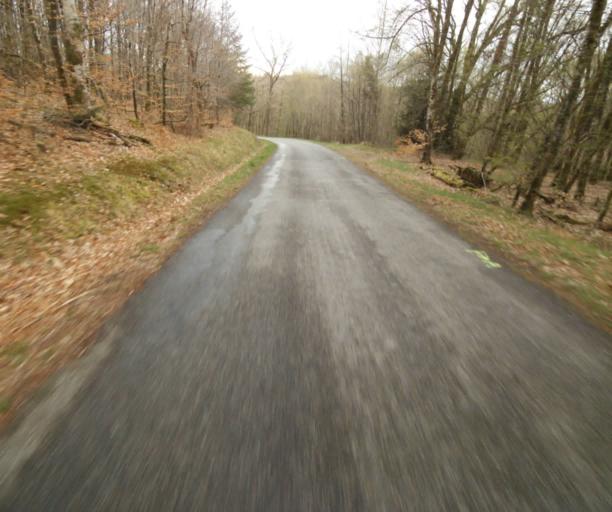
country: FR
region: Limousin
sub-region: Departement de la Correze
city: Argentat
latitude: 45.2273
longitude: 1.9834
